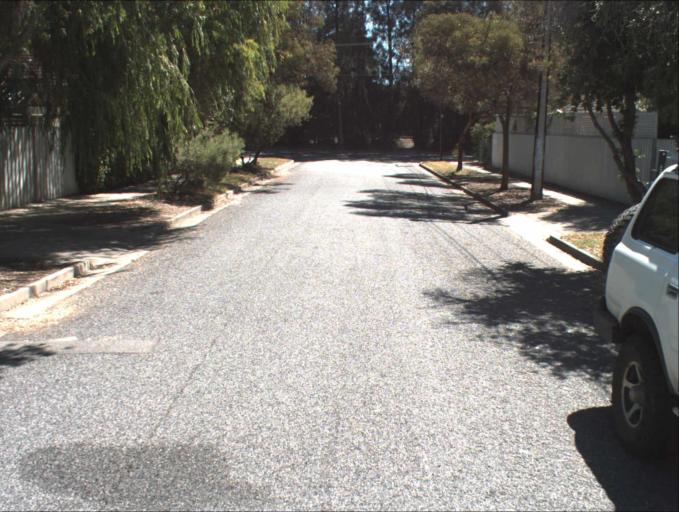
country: AU
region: South Australia
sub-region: Port Adelaide Enfield
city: Birkenhead
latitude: -34.8111
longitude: 138.4998
